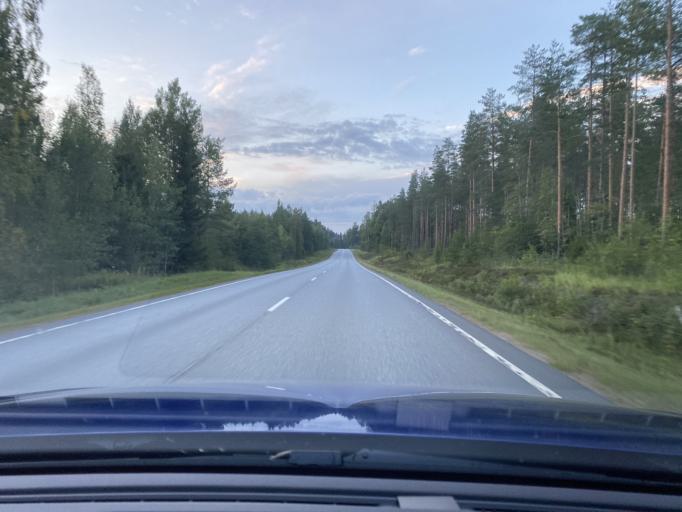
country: FI
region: Satakunta
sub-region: Pohjois-Satakunta
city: Honkajoki
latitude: 62.0391
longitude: 22.2416
